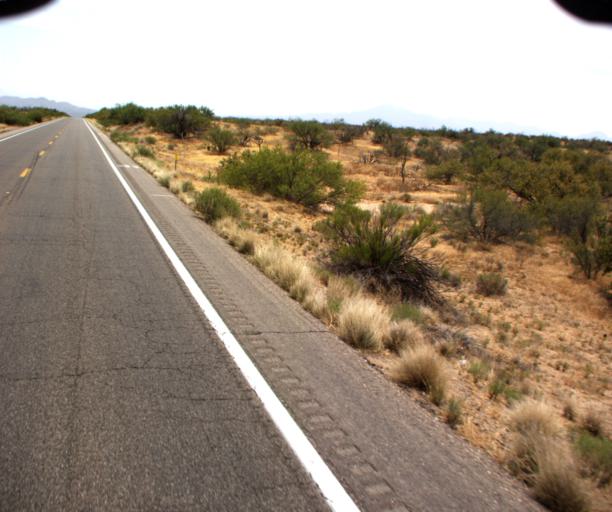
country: US
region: Arizona
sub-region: Gila County
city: Peridot
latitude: 33.3152
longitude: -110.5200
